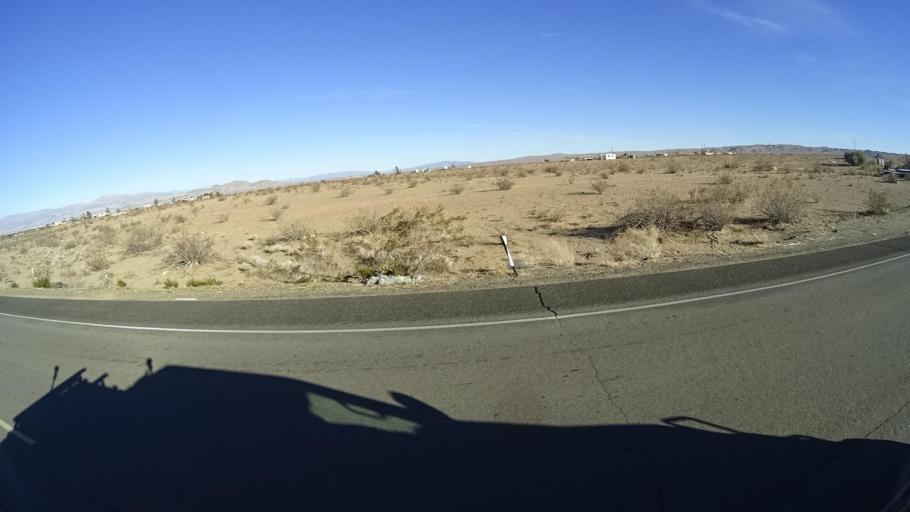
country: US
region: California
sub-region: Kern County
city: China Lake Acres
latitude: 35.6112
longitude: -117.7230
